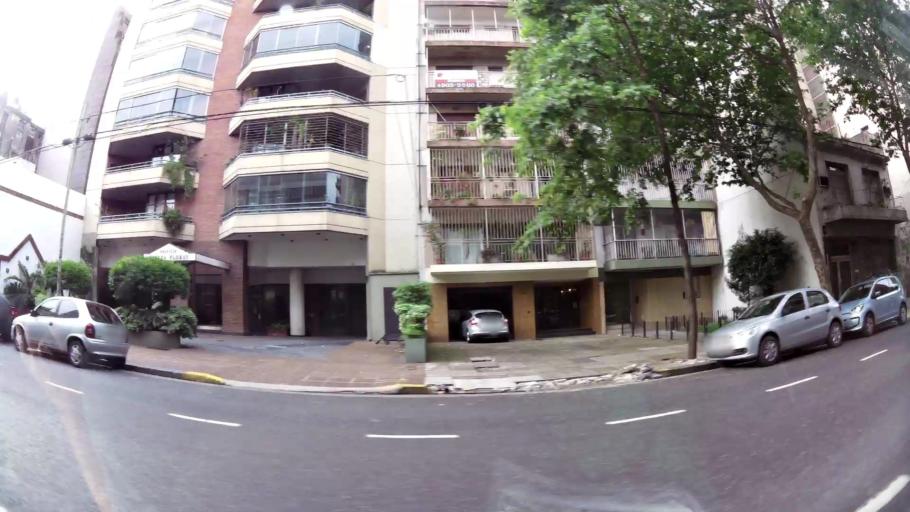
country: AR
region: Buenos Aires F.D.
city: Villa Santa Rita
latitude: -34.6309
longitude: -58.4612
